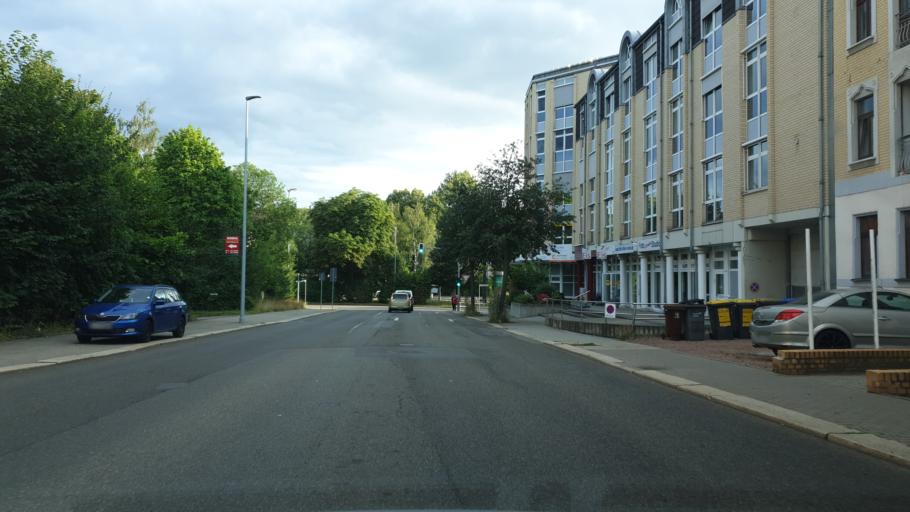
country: DE
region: Saxony
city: Hilbersdorf
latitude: 50.8321
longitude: 12.9541
